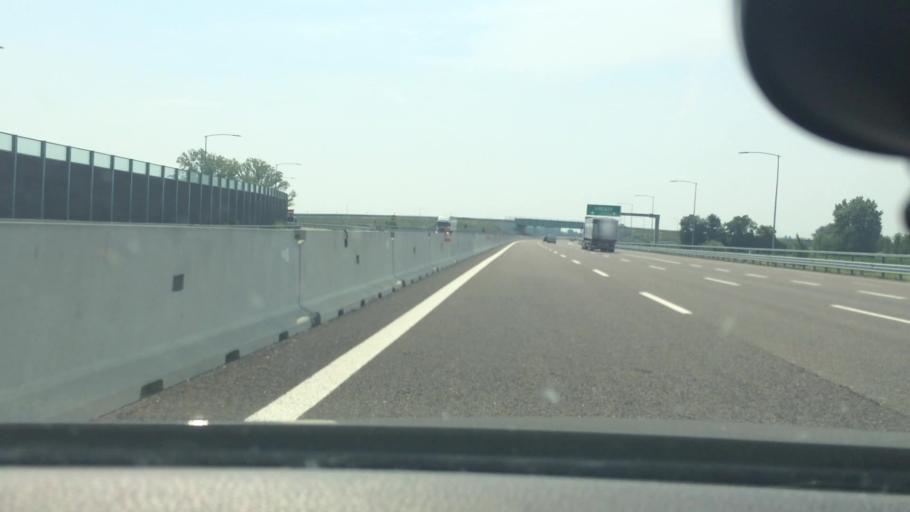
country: IT
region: Lombardy
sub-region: Citta metropolitana di Milano
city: Liscate
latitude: 45.4701
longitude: 9.4319
